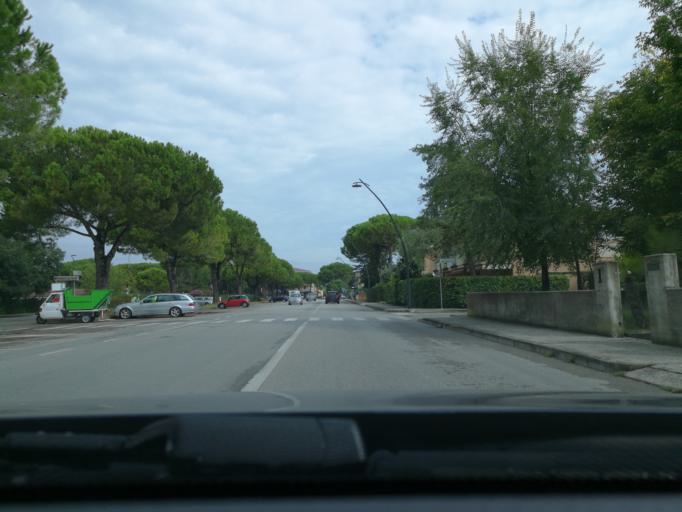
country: IT
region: Veneto
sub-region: Provincia di Venezia
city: Bibione
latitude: 45.6406
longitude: 13.0547
